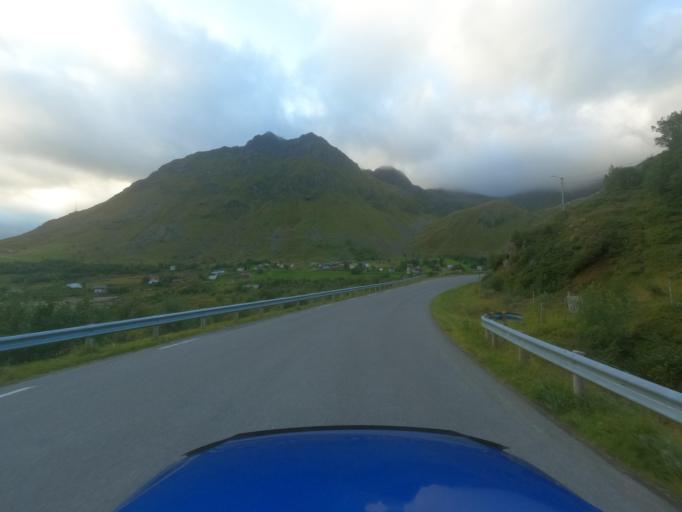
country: NO
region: Nordland
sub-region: Vestvagoy
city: Evjen
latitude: 68.2477
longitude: 13.6558
